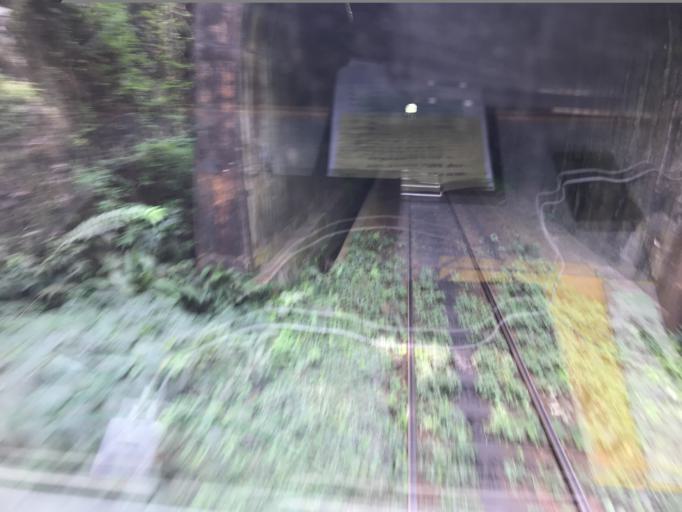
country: CM
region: Centre
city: Eseka
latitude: 3.5746
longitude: 10.8837
